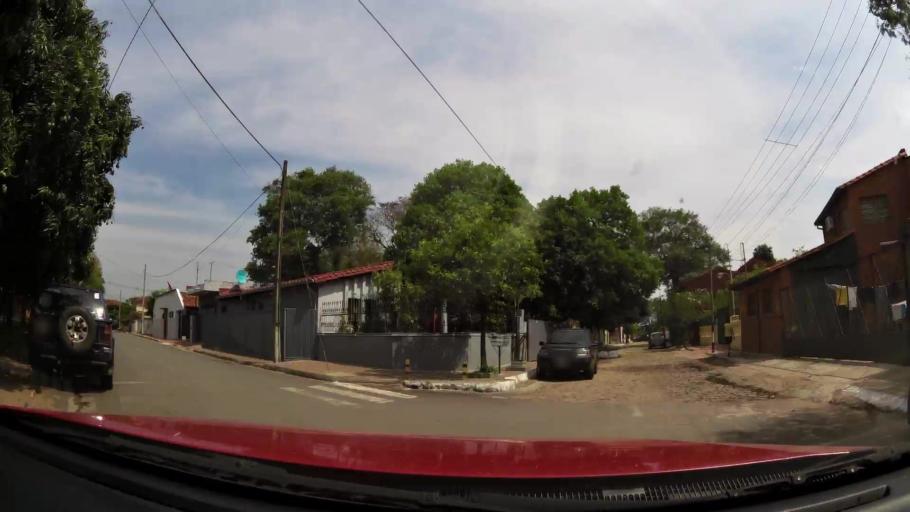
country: PY
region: Asuncion
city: Asuncion
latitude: -25.2642
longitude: -57.5877
